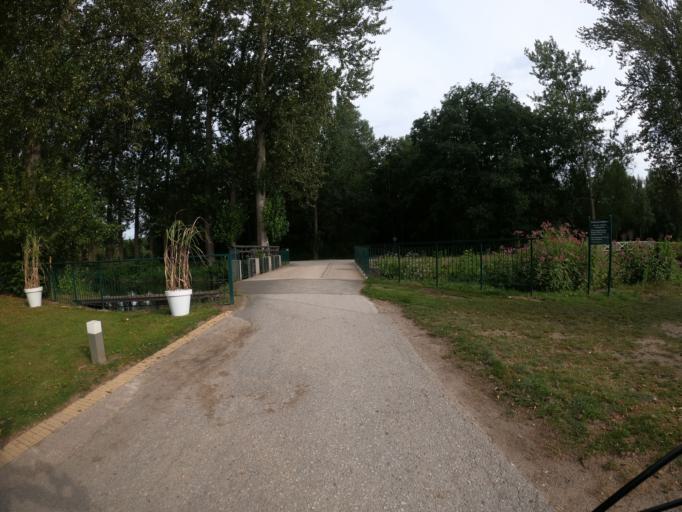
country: DE
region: North Rhine-Westphalia
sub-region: Regierungsbezirk Arnsberg
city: Lippstadt
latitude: 51.6952
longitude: 8.3283
